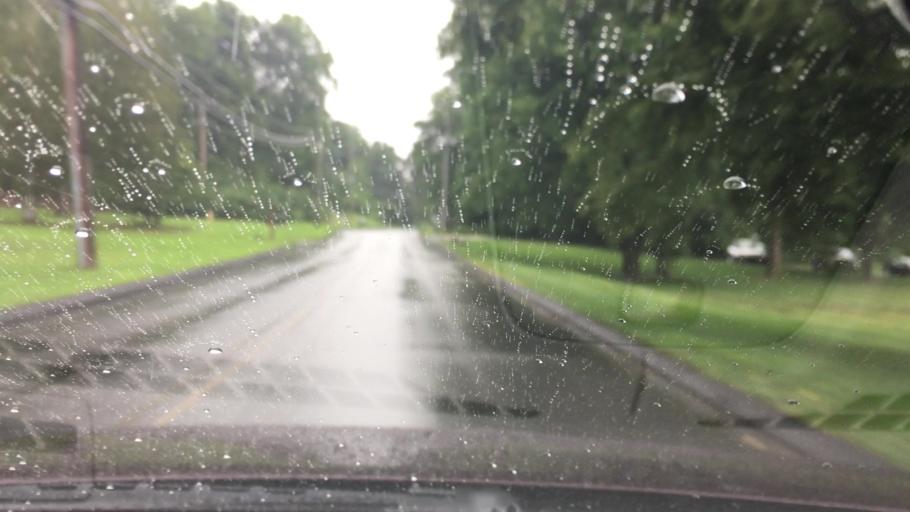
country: US
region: Connecticut
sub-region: New Haven County
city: Cheshire Village
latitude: 41.5373
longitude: -72.9031
